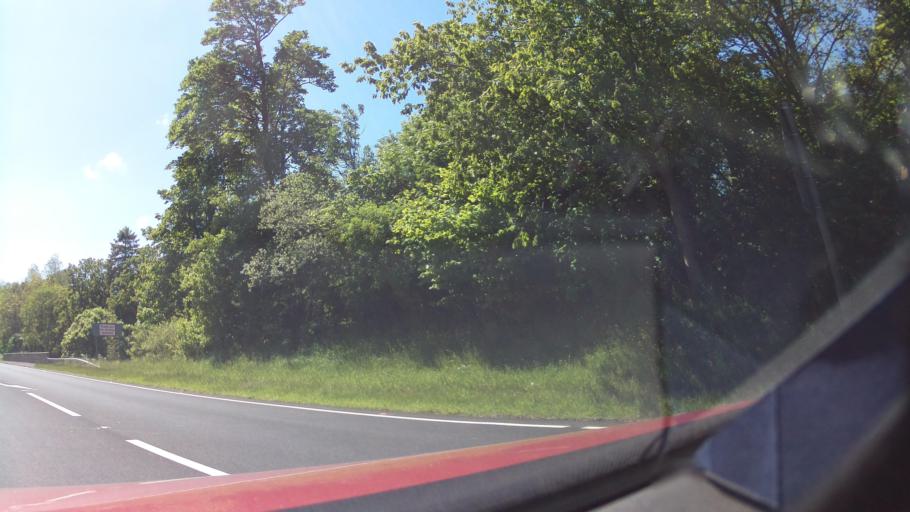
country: GB
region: Scotland
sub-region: The Scottish Borders
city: Hawick
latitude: 55.3379
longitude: -2.9390
